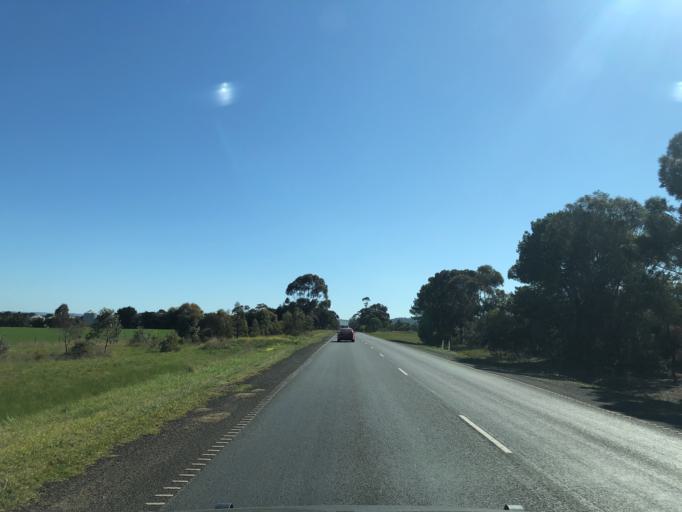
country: AU
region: Victoria
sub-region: Melton
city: Kurunjang
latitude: -37.6253
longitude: 144.6368
